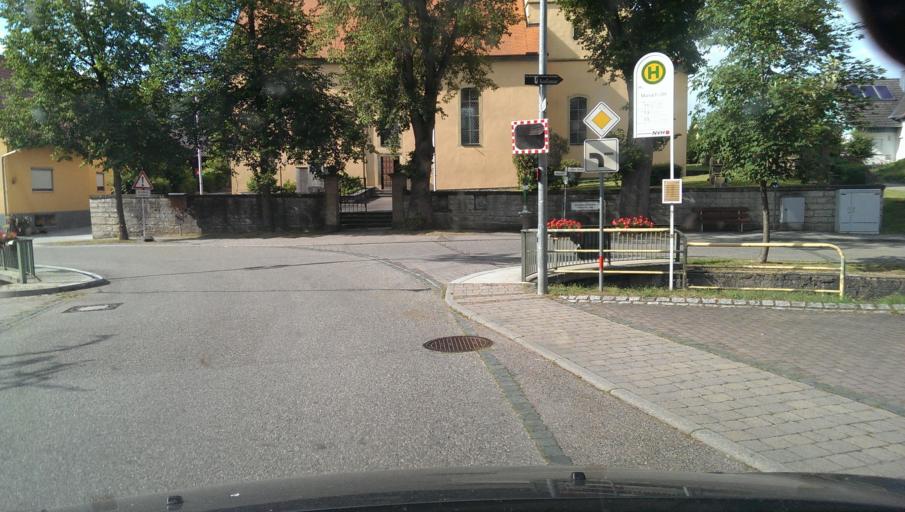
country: DE
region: Baden-Wuerttemberg
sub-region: Regierungsbezirk Stuttgart
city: Krautheim
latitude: 49.3599
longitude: 9.6012
